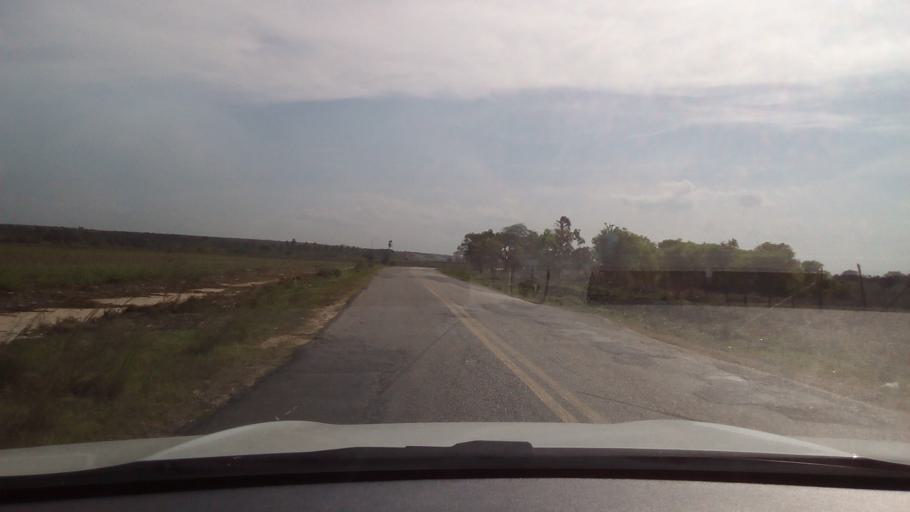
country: BR
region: Rio Grande do Norte
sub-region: Goianinha
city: Goianinha
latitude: -6.2551
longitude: -35.1935
